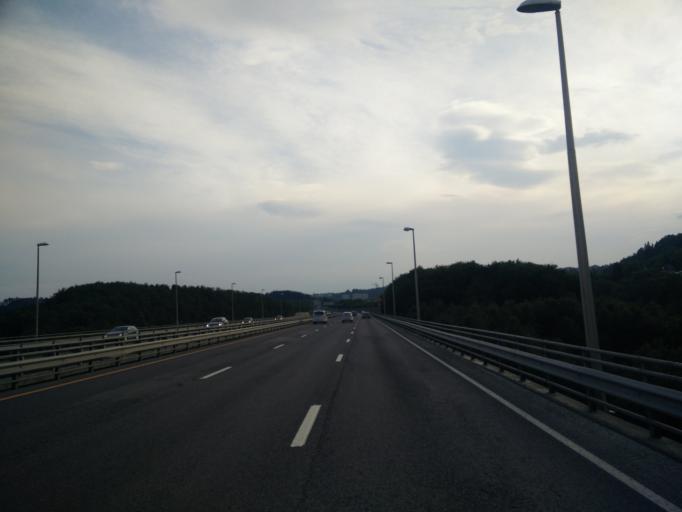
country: NO
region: Sor-Trondelag
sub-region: Trondheim
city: Trondheim
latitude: 63.3930
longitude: 10.3860
